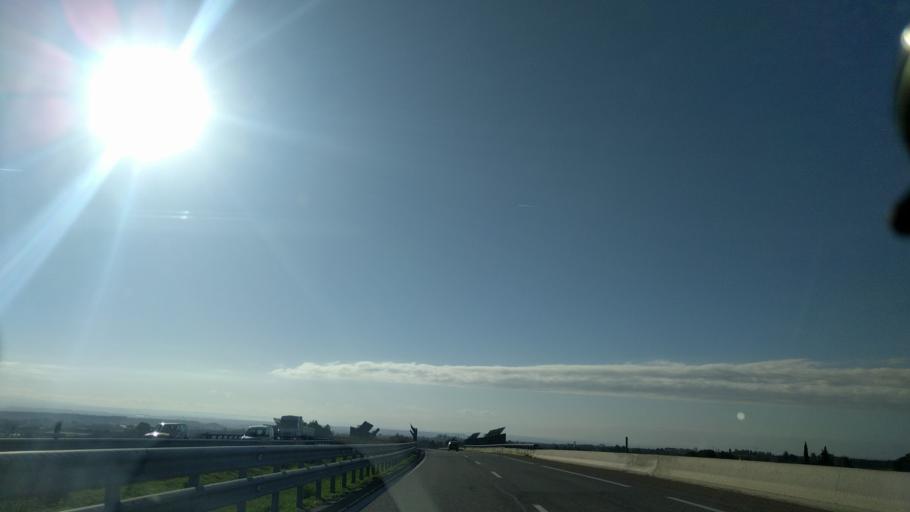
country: ES
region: Catalonia
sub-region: Provincia de Lleida
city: Alpicat
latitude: 41.6261
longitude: 0.5513
